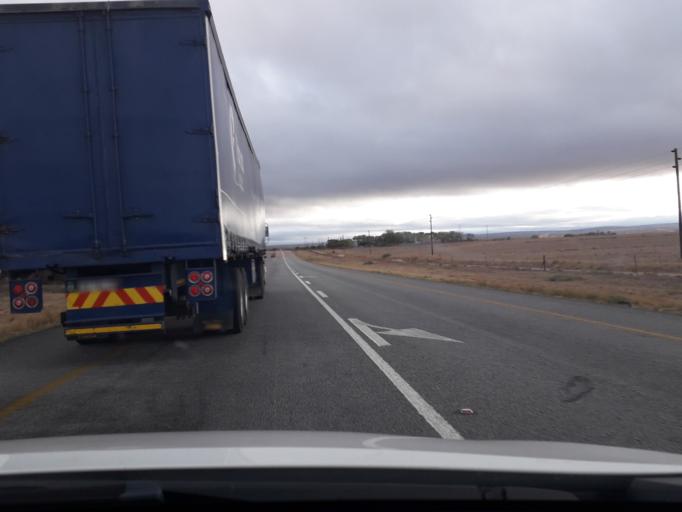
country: ZA
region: Limpopo
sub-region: Capricorn District Municipality
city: Polokwane
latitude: -23.7306
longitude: 29.5836
